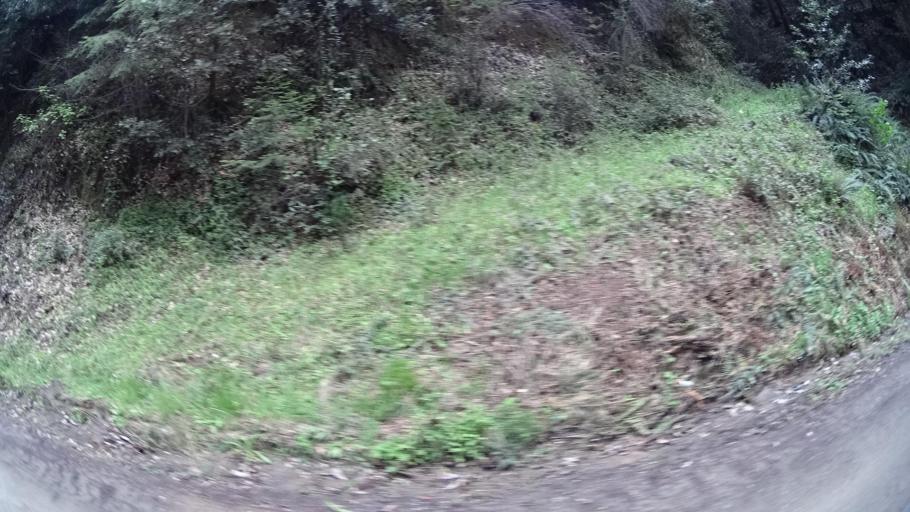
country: US
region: California
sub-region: Humboldt County
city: Blue Lake
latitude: 40.7640
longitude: -123.9543
